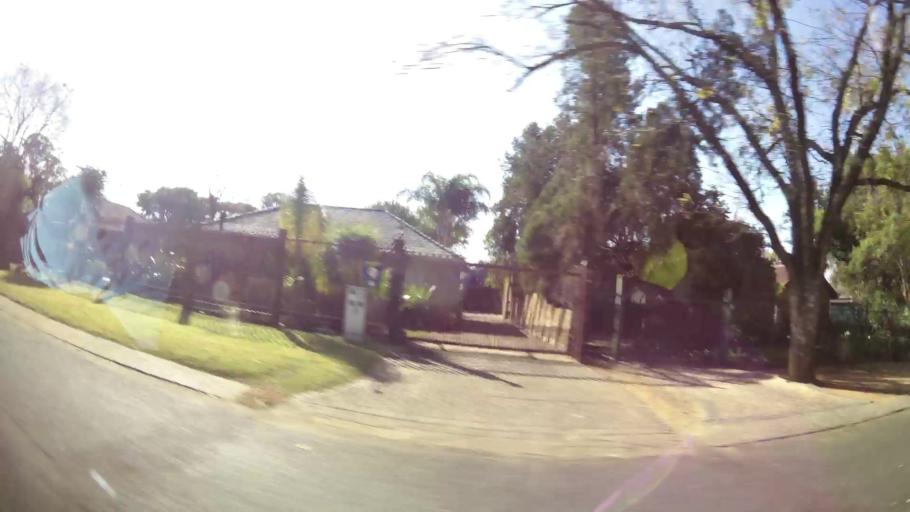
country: ZA
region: Gauteng
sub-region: City of Tshwane Metropolitan Municipality
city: Pretoria
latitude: -25.7301
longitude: 28.2560
